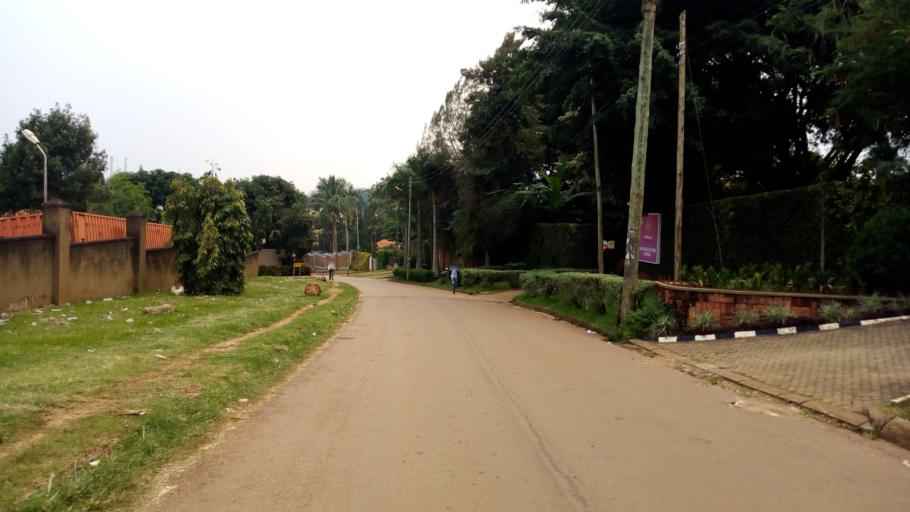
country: UG
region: Central Region
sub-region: Wakiso District
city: Kireka
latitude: 0.3206
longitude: 32.6269
